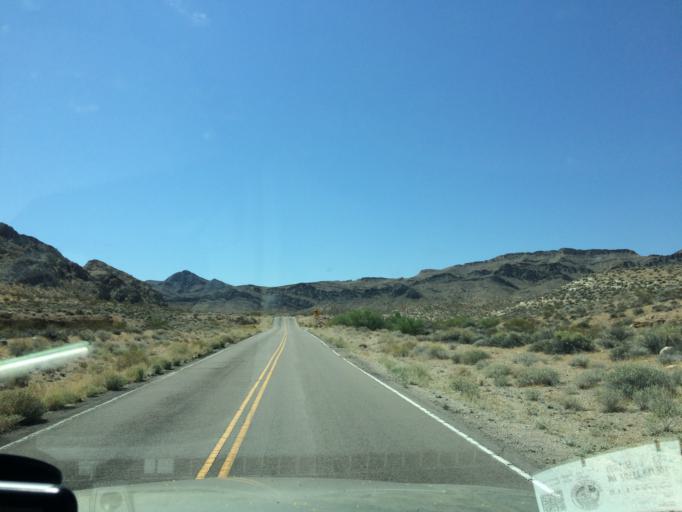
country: US
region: Nevada
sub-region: Clark County
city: Moapa Valley
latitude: 36.4291
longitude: -114.6272
